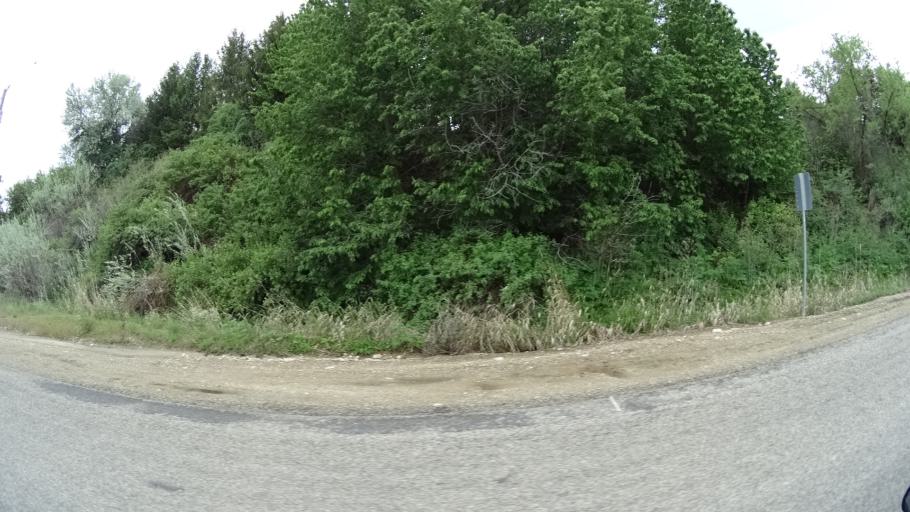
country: US
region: Idaho
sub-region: Ada County
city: Star
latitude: 43.6696
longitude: -116.4743
